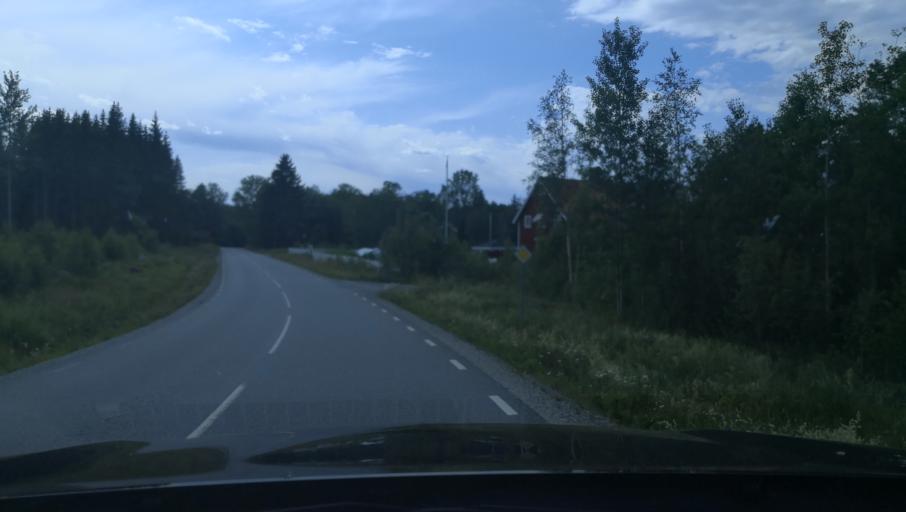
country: SE
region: Vaestmanland
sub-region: Norbergs Kommun
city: Norberg
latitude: 59.9758
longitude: 16.0331
